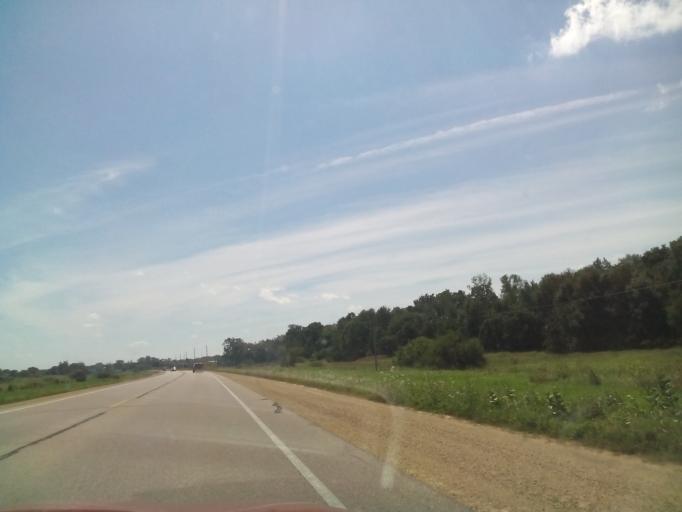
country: US
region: Wisconsin
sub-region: Green County
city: Monticello
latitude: 42.7543
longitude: -89.6084
